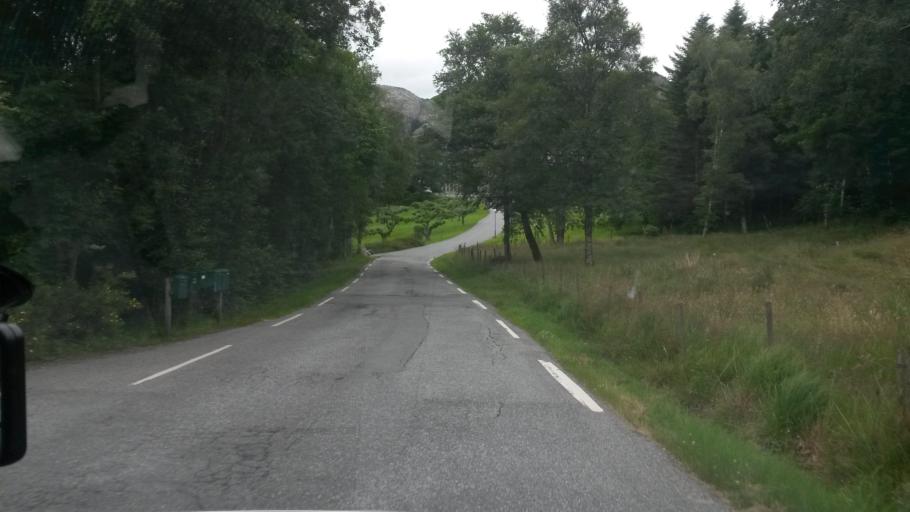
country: NO
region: Rogaland
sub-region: Sandnes
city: Sandnes
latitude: 58.8973
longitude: 5.7768
